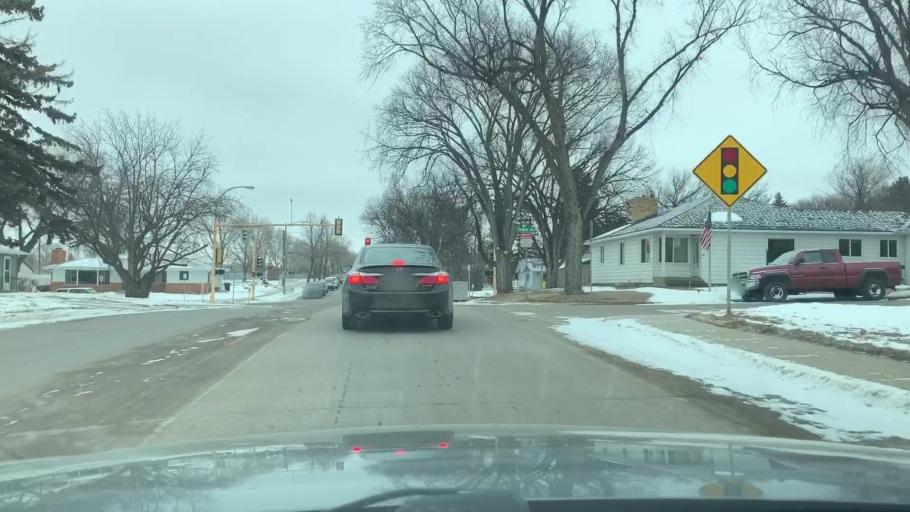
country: US
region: North Dakota
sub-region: Burleigh County
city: Bismarck
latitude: 46.8161
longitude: -100.7942
